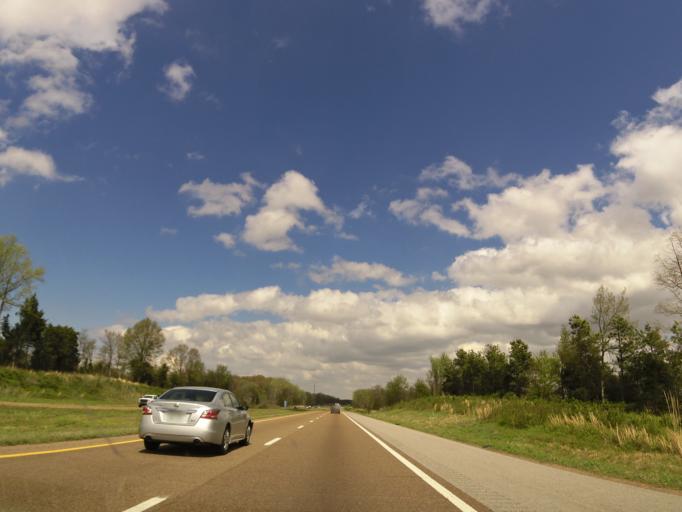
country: US
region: Tennessee
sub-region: Fayette County
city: Hickory Withe
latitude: 35.3244
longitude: -89.5650
